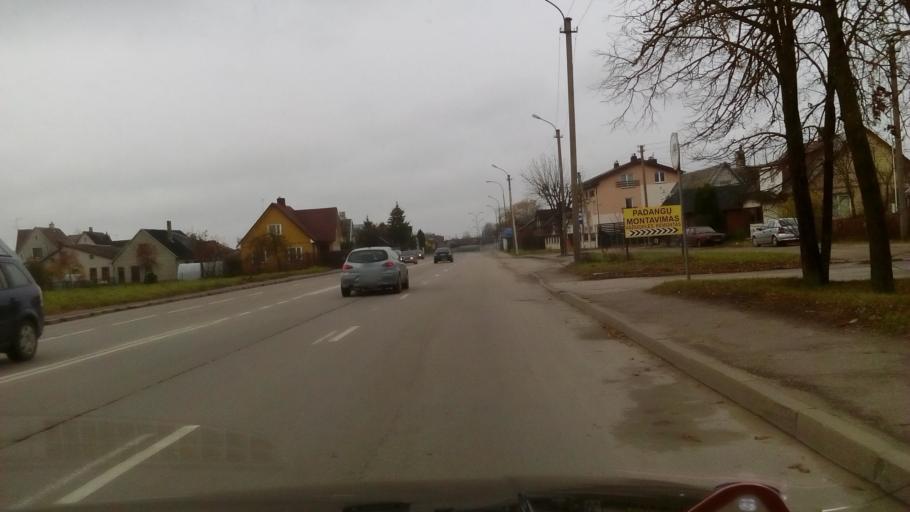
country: LT
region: Marijampoles apskritis
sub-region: Marijampole Municipality
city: Marijampole
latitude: 54.5543
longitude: 23.3699
